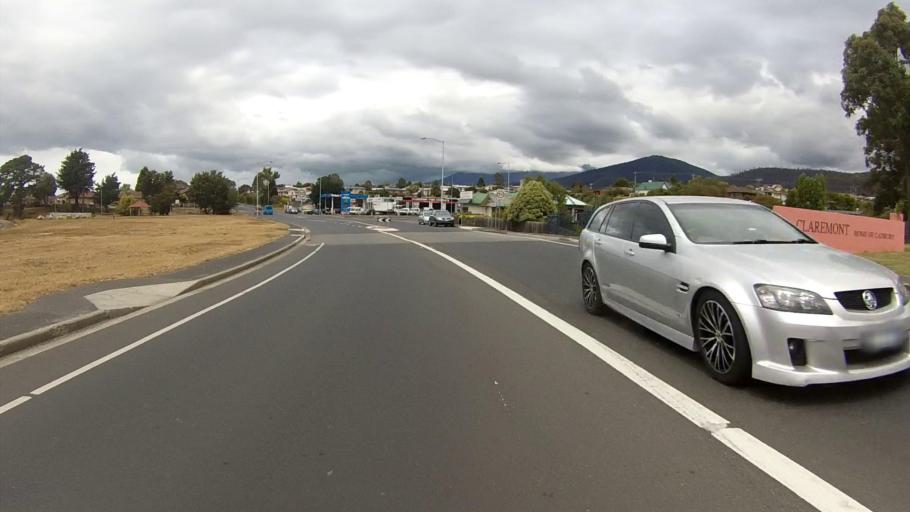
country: AU
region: Tasmania
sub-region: Glenorchy
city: Claremont
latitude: -42.7860
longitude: 147.2518
